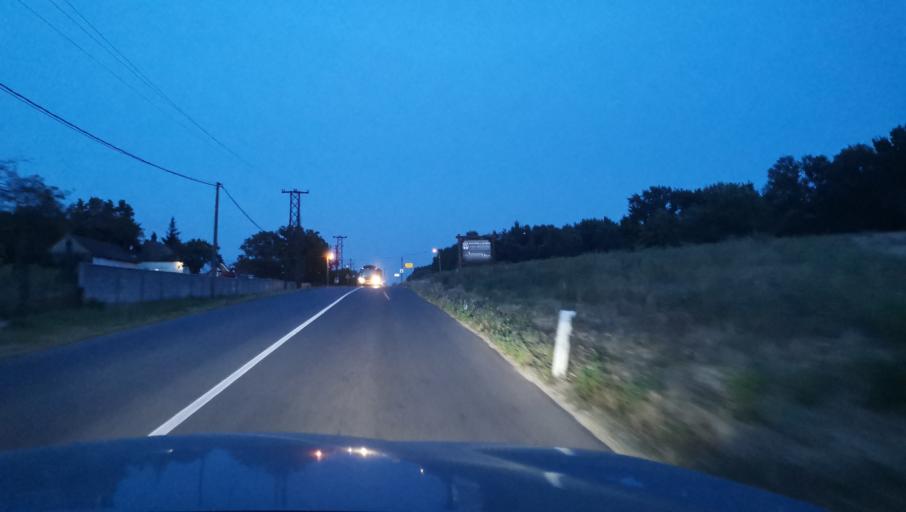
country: RS
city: Boljevci
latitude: 44.7187
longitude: 20.2213
